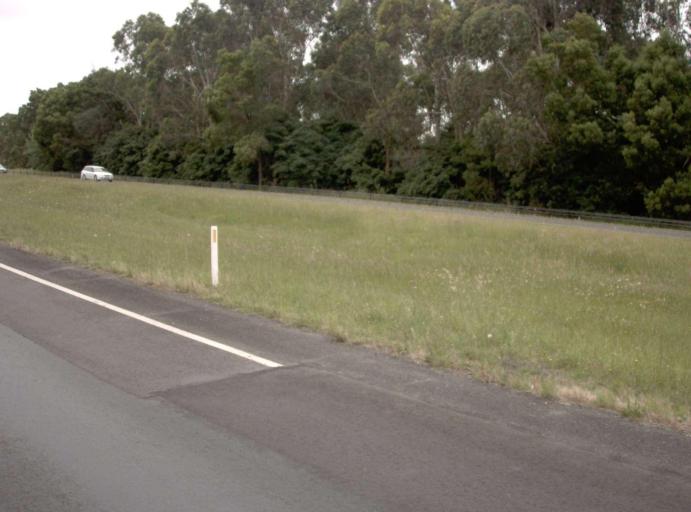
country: AU
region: Victoria
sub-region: Baw Baw
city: Warragul
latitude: -38.1168
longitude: 145.8647
